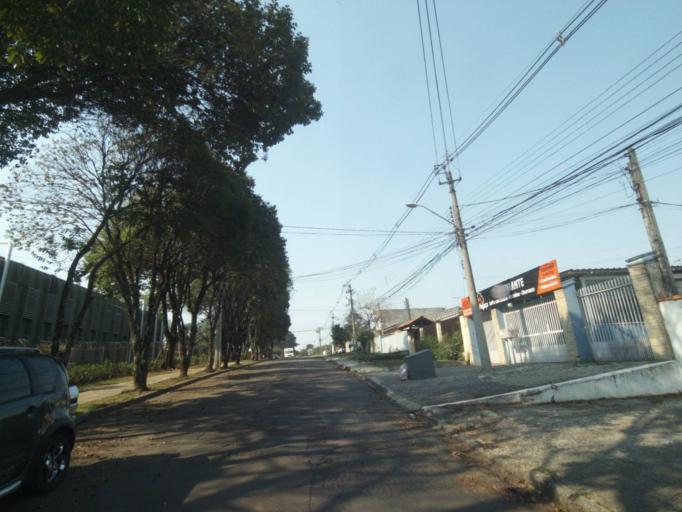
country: BR
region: Parana
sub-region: Curitiba
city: Curitiba
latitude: -25.5028
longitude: -49.2793
